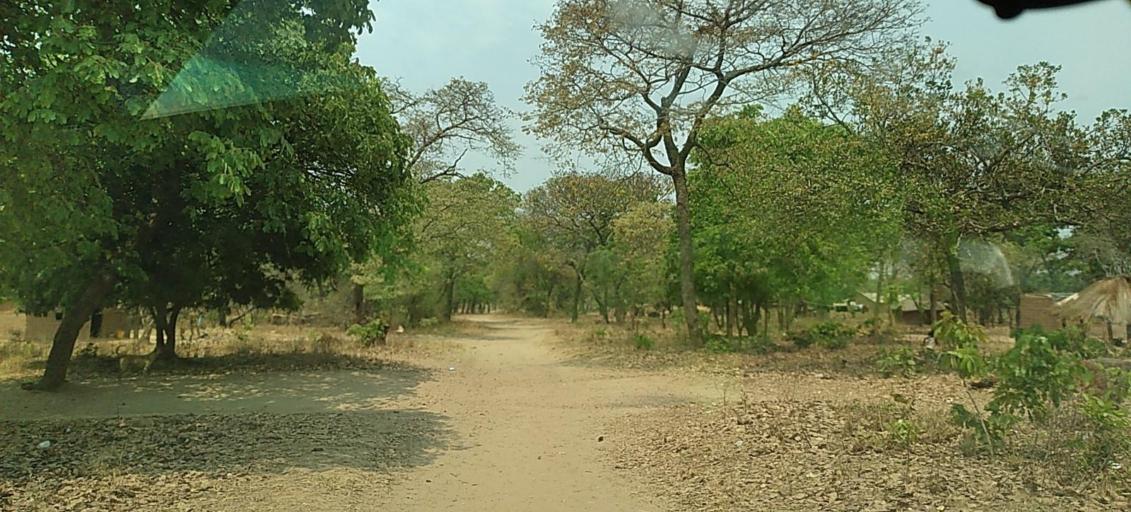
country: ZM
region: North-Western
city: Kabompo
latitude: -13.5673
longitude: 24.4424
